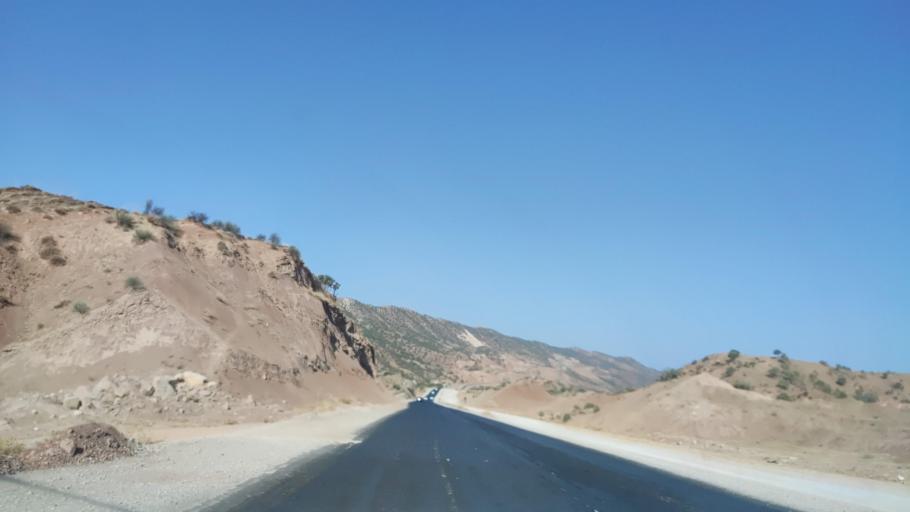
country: IQ
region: Arbil
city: Shaqlawah
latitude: 36.4298
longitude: 44.3341
